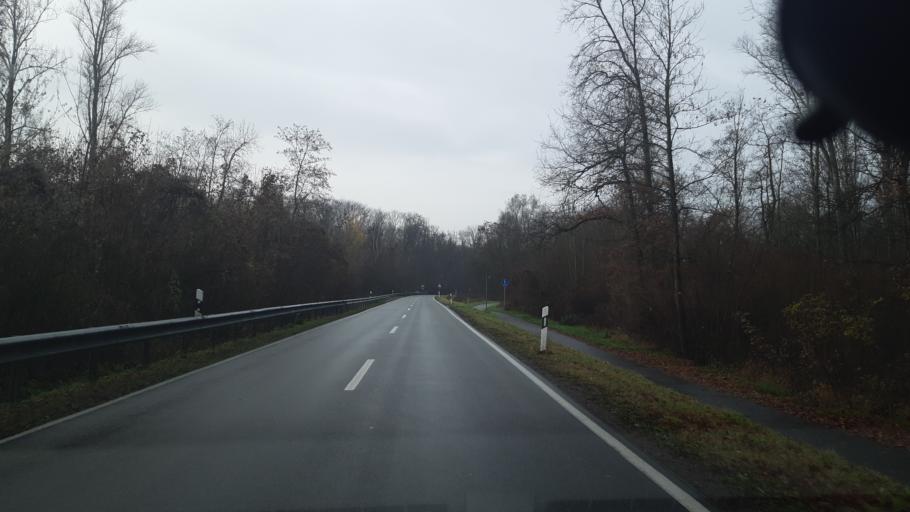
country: DE
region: Rheinland-Pfalz
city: Altrip
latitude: 49.4010
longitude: 8.4798
